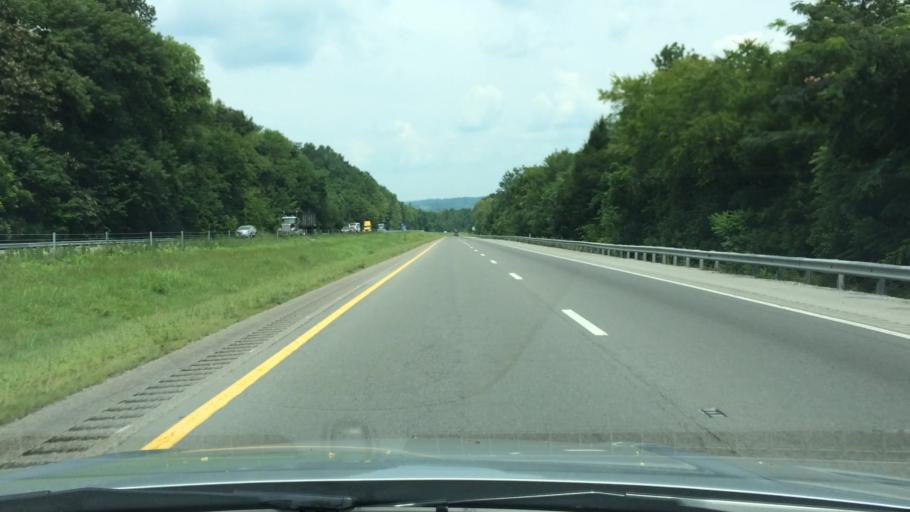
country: US
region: Tennessee
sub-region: Marshall County
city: Cornersville
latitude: 35.2624
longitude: -86.8848
